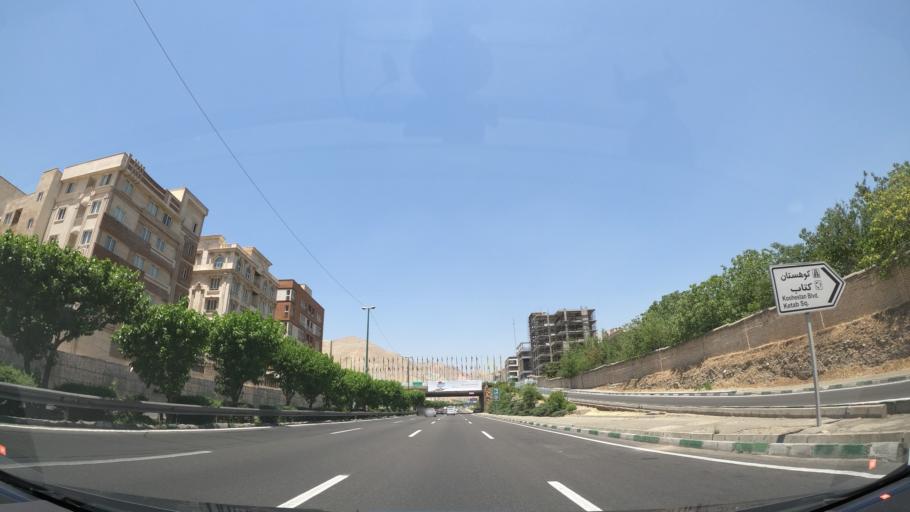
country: IR
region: Tehran
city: Tajrish
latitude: 35.7742
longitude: 51.3447
